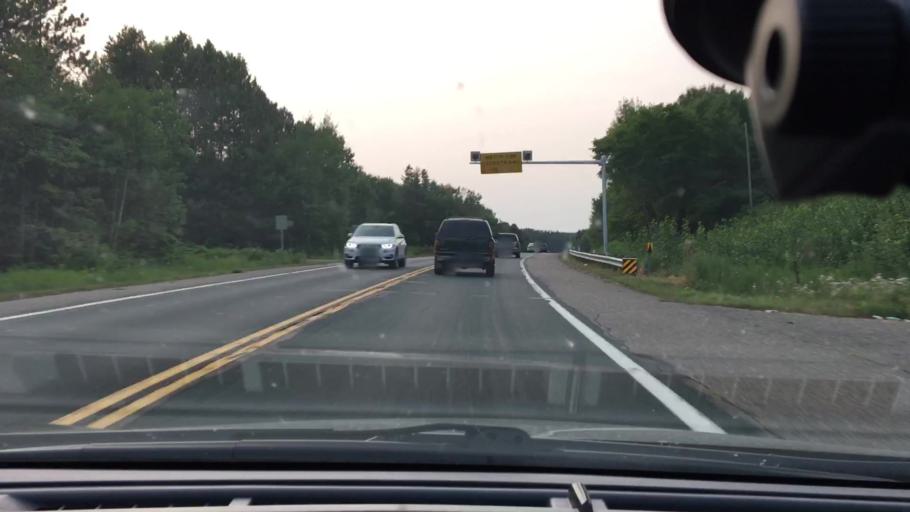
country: US
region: Minnesota
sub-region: Mille Lacs County
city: Vineland
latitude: 46.2042
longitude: -93.7830
